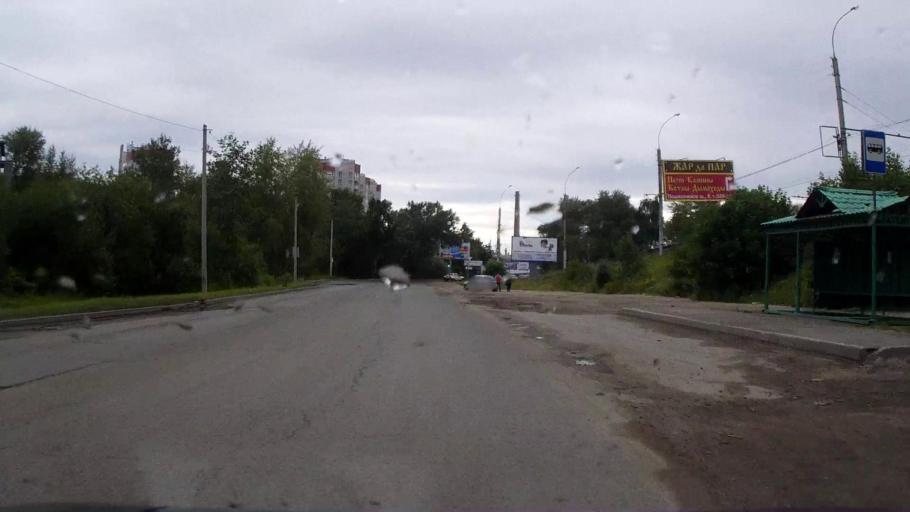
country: RU
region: Vologda
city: Vologda
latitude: 59.2056
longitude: 39.8753
